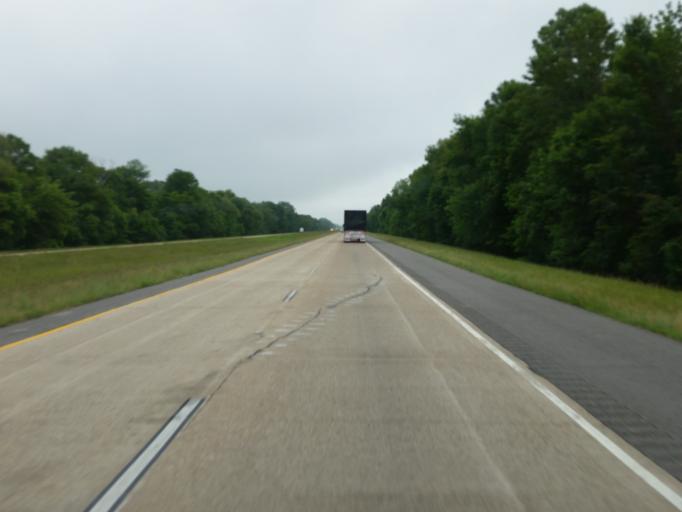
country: US
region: Louisiana
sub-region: Madison Parish
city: Tallulah
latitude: 32.3551
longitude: -91.1001
